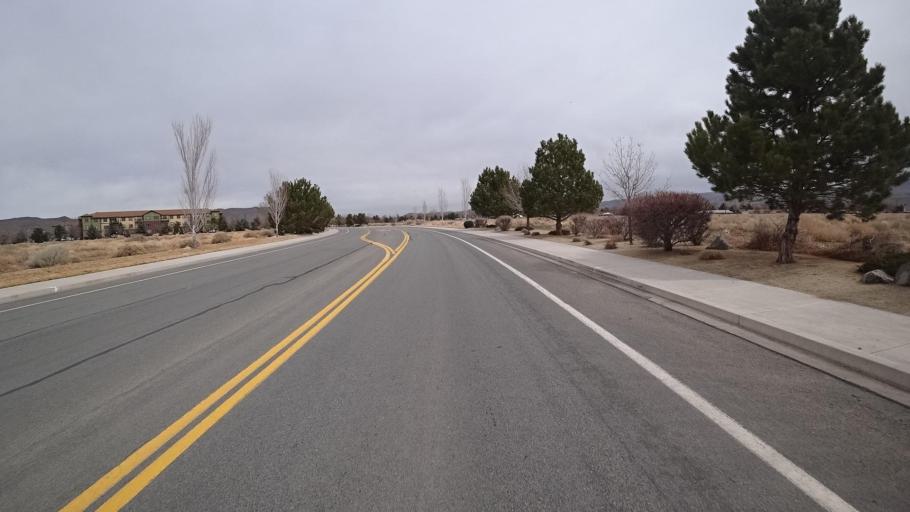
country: US
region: Nevada
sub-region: Washoe County
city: Spanish Springs
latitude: 39.6429
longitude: -119.7188
